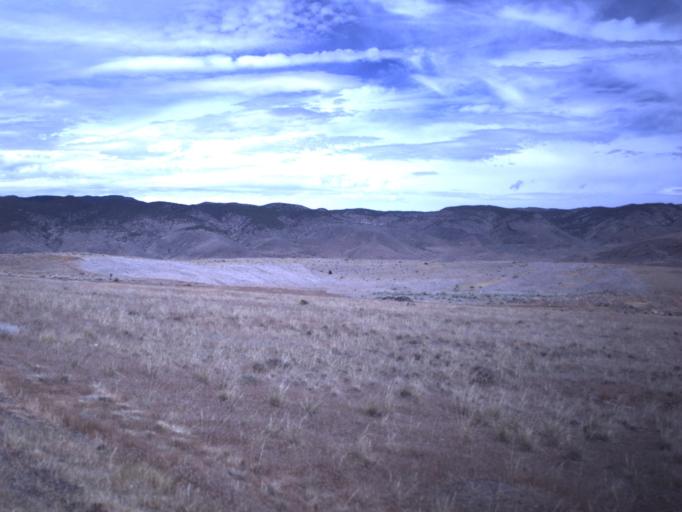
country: US
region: Utah
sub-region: Sevier County
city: Monroe
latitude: 38.6321
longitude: -112.1739
